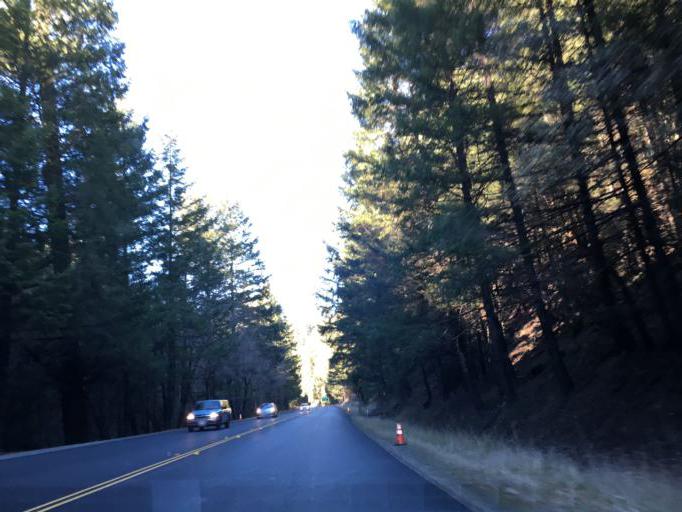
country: US
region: California
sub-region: Mendocino County
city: Laytonville
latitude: 39.7997
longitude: -123.5429
